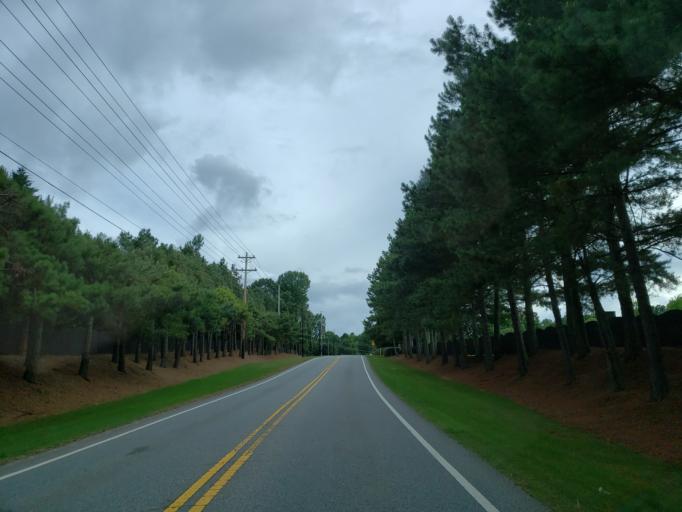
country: US
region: Georgia
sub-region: Cherokee County
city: Ball Ground
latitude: 34.2368
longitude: -84.3551
